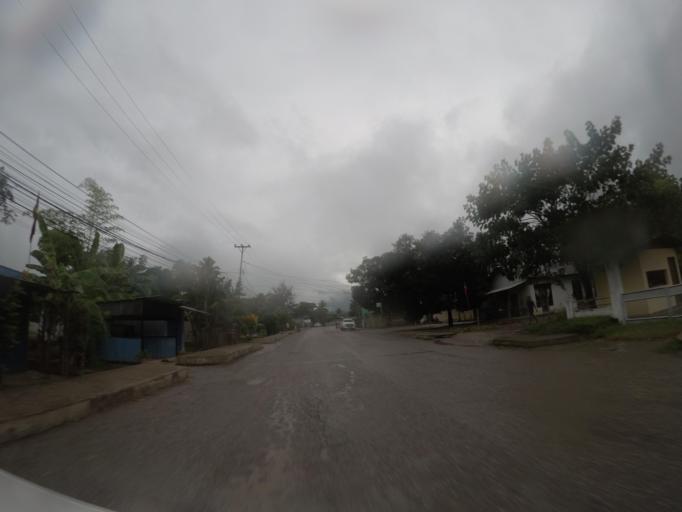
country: TL
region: Bobonaro
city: Maliana
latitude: -8.9889
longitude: 125.2134
